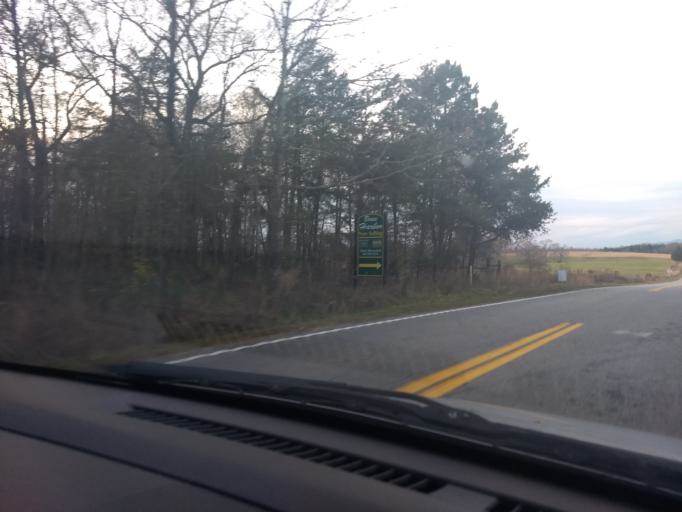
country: US
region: South Carolina
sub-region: Greenville County
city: Greer
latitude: 34.9951
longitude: -82.2072
